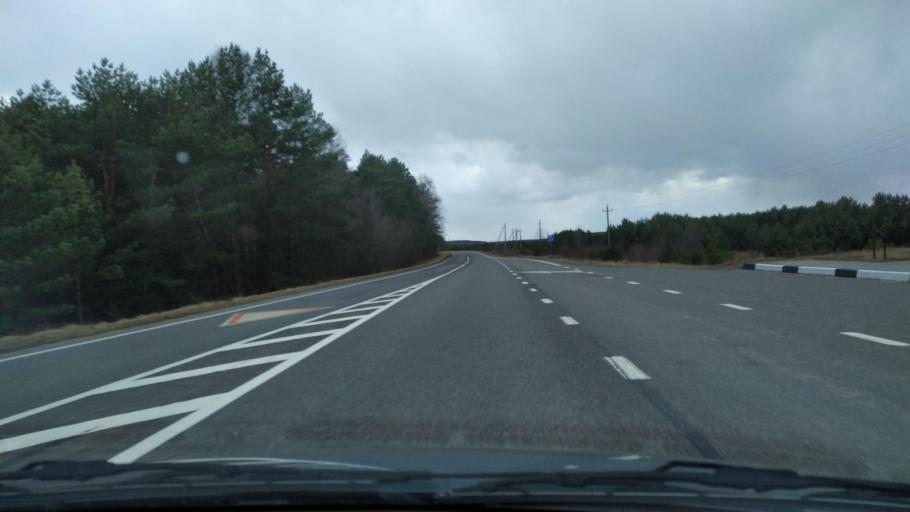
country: BY
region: Brest
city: Kamyanyets
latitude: 52.4007
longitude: 24.0054
